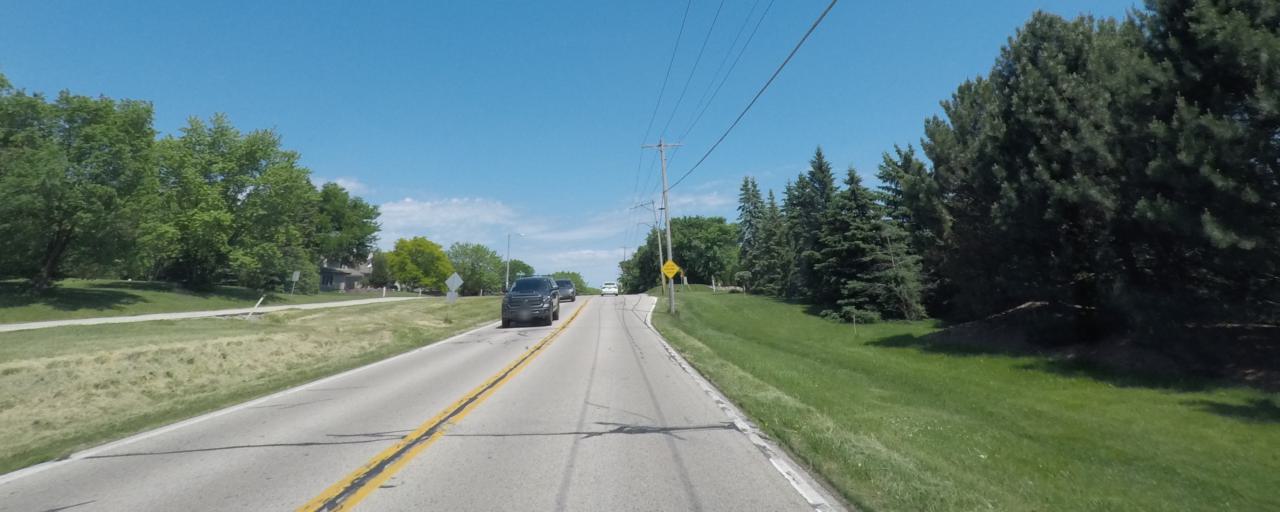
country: US
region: Wisconsin
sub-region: Waukesha County
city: New Berlin
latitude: 42.9443
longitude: -88.0880
